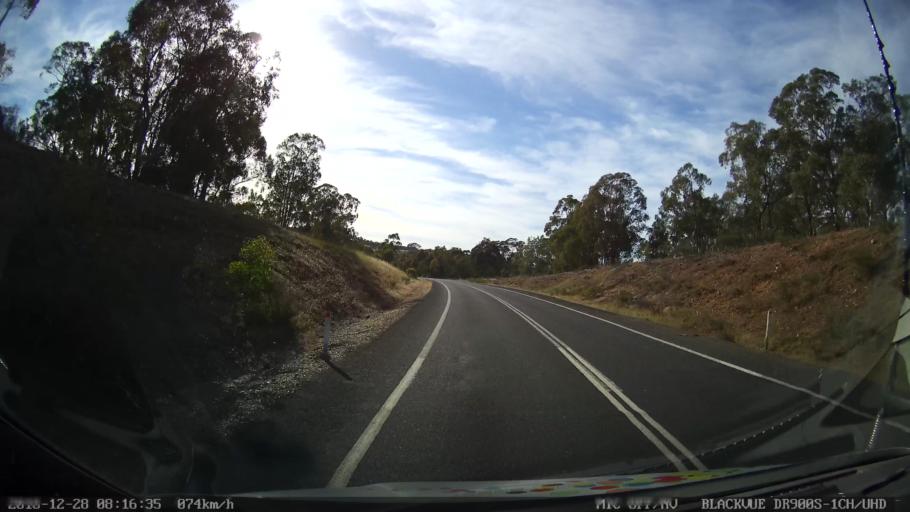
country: AU
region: New South Wales
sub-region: Blayney
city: Blayney
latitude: -33.8349
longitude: 149.3303
